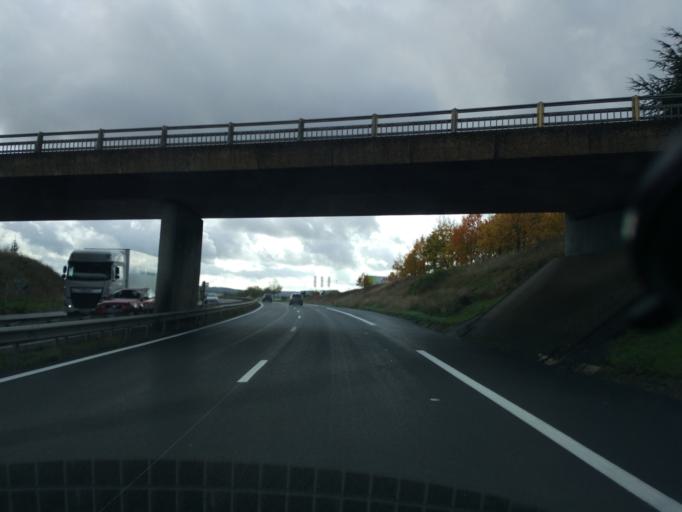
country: FR
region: Poitou-Charentes
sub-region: Departement de la Charente
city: Champniers
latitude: 45.7704
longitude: 0.1891
